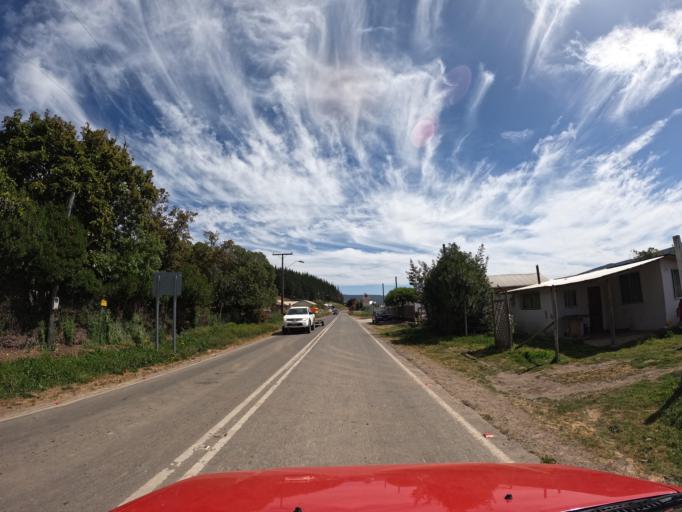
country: CL
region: Maule
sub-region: Provincia de Talca
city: Constitucion
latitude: -35.0224
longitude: -72.0411
